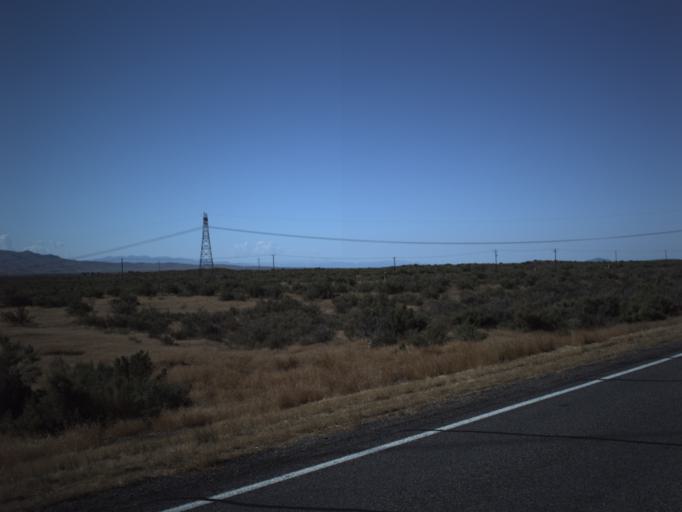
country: US
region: Utah
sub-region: Millard County
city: Delta
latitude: 39.4924
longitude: -112.4008
